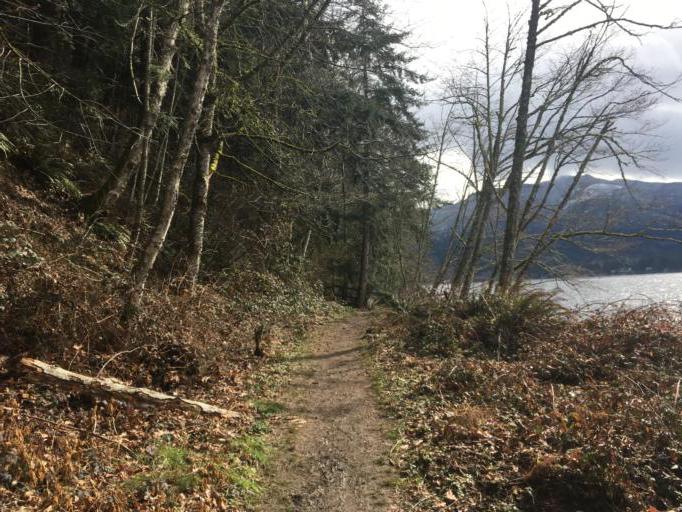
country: US
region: Washington
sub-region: Whatcom County
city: Sudden Valley
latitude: 48.6893
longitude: -122.2898
